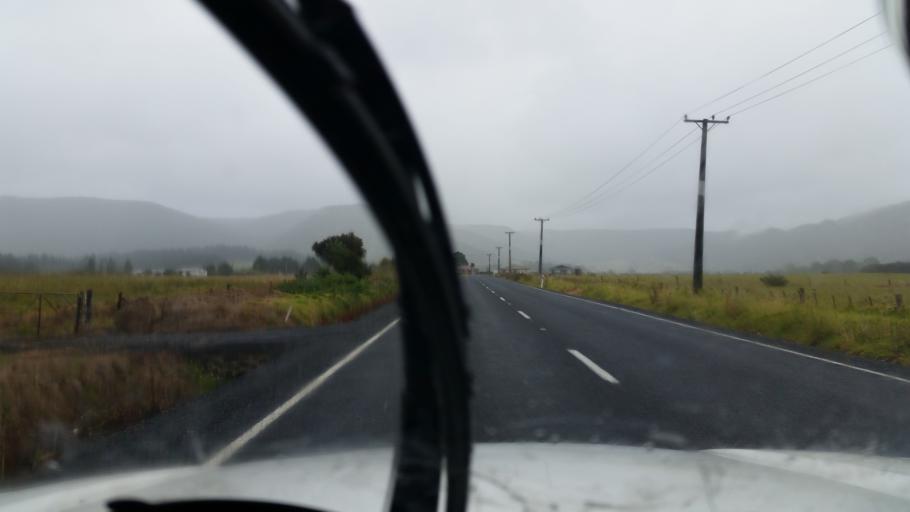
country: NZ
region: Northland
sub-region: Far North District
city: Ahipara
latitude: -35.1780
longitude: 173.1714
